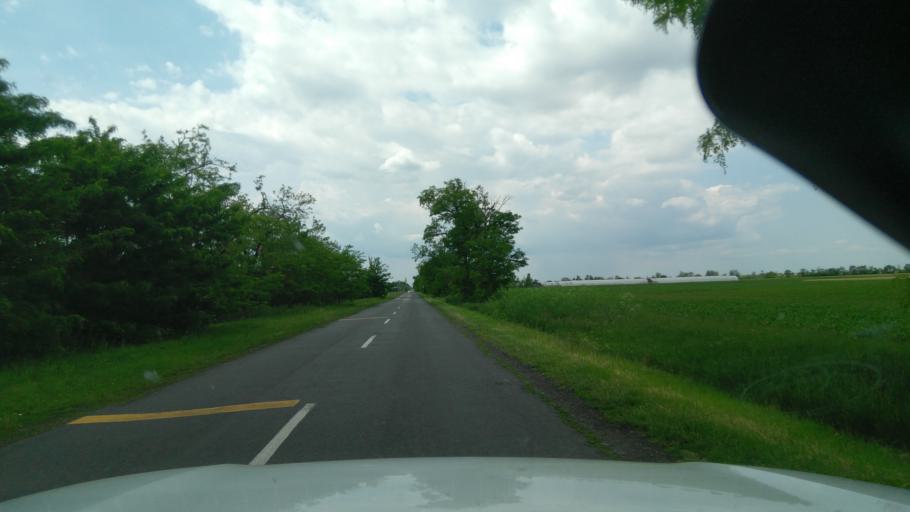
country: HU
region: Bekes
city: Magyarbanhegyes
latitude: 46.4435
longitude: 20.9847
